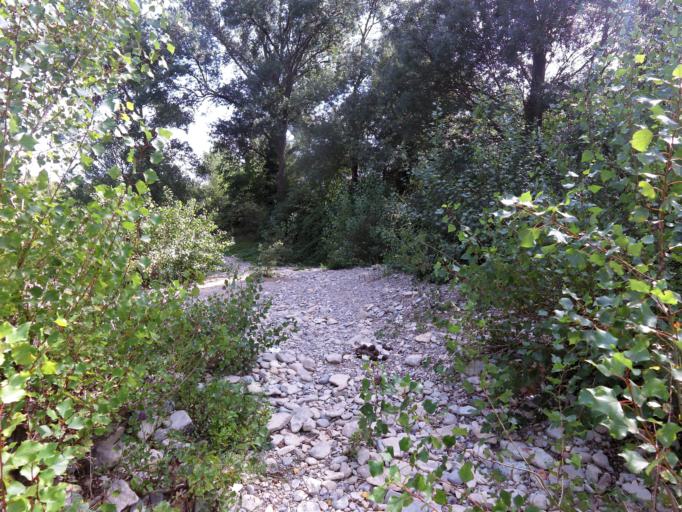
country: FR
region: Languedoc-Roussillon
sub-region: Departement du Gard
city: Sommieres
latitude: 43.8346
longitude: 4.0680
